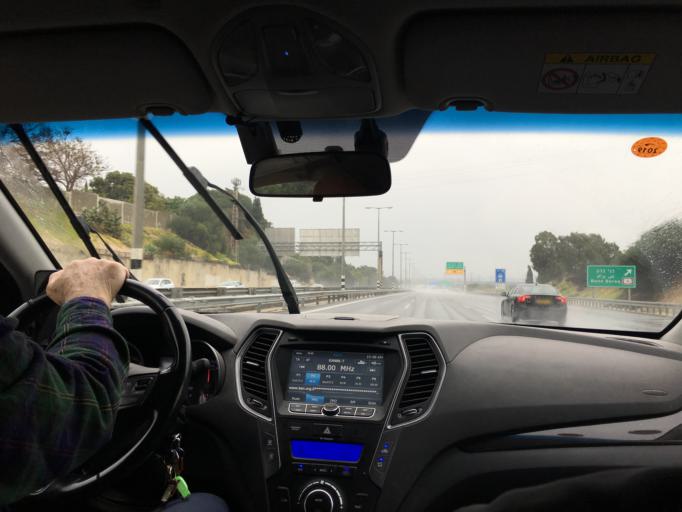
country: IL
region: Tel Aviv
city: Ramat HaSharon
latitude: 32.1292
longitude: 34.8449
